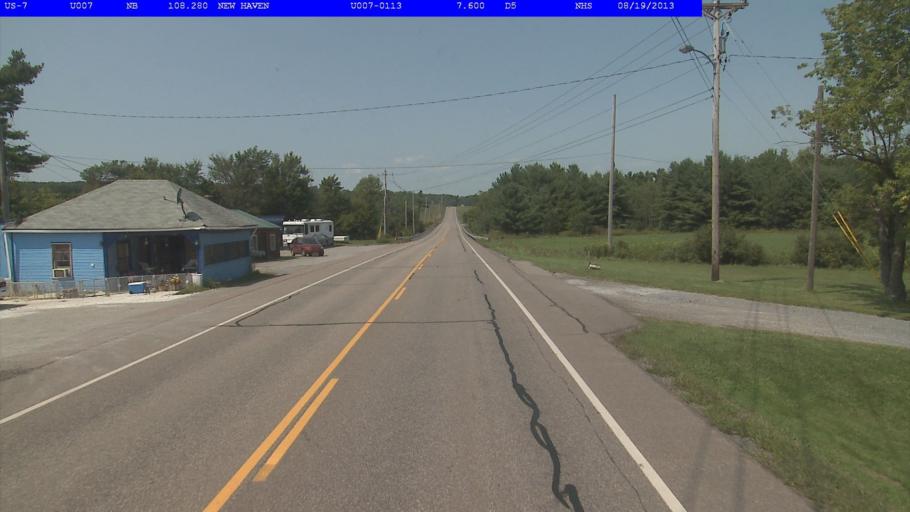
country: US
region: Vermont
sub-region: Addison County
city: Vergennes
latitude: 44.1467
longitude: -73.2089
